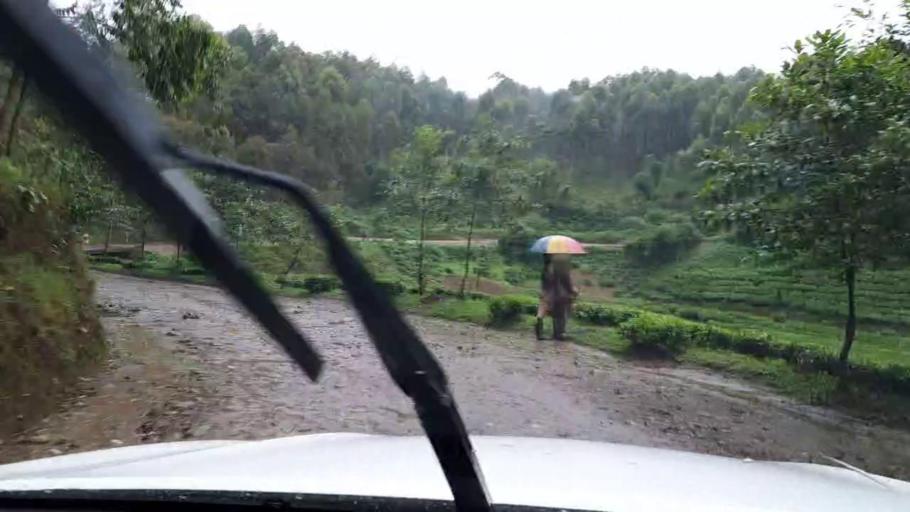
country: RW
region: Western Province
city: Cyangugu
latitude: -2.4641
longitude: 29.0339
